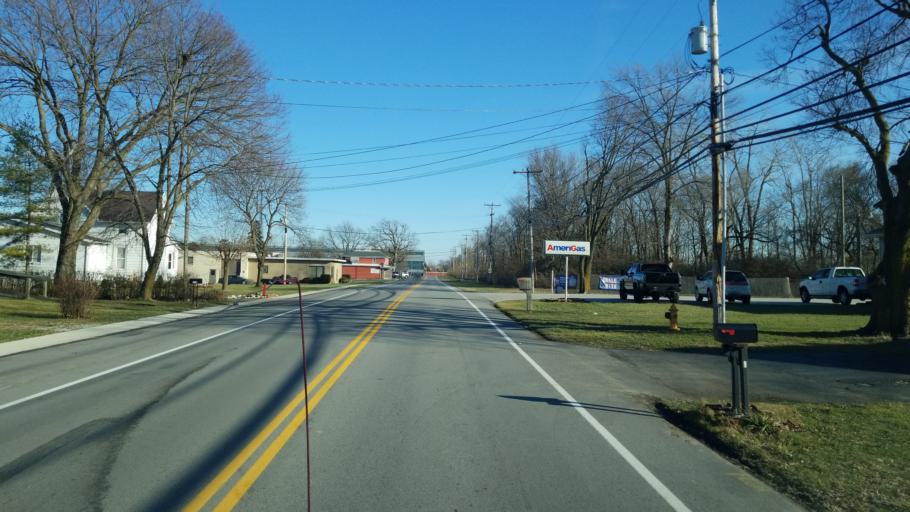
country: US
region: Ohio
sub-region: Sandusky County
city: Stony Prairie
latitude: 41.3494
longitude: -83.1411
